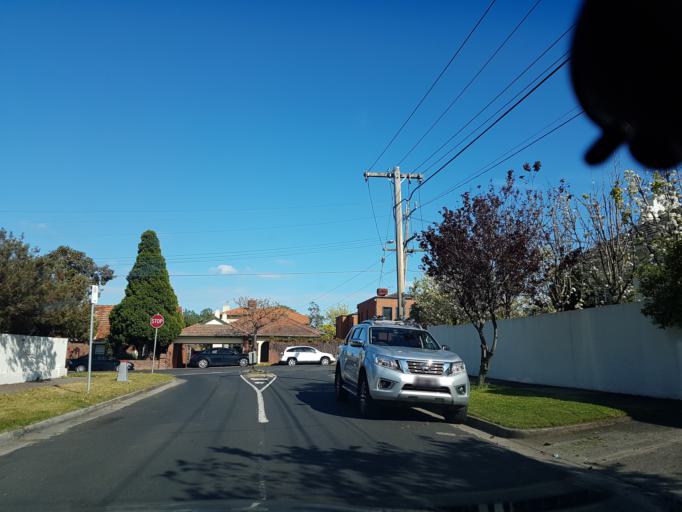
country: AU
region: Victoria
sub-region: Bayside
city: Brighton East
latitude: -37.9086
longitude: 145.0252
